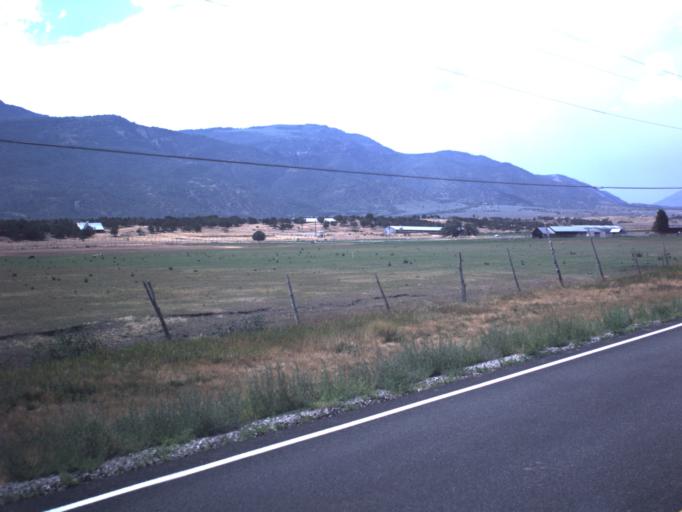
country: US
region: Utah
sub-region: Sanpete County
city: Fountain Green
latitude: 39.5999
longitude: -111.6215
